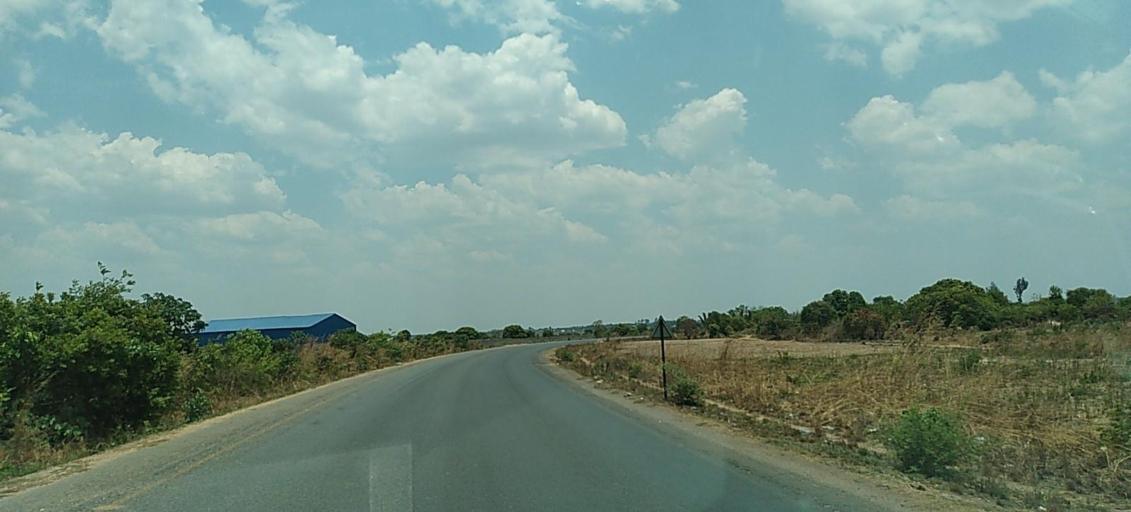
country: ZM
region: Central
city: Kapiri Mposhi
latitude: -13.8949
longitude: 28.6645
